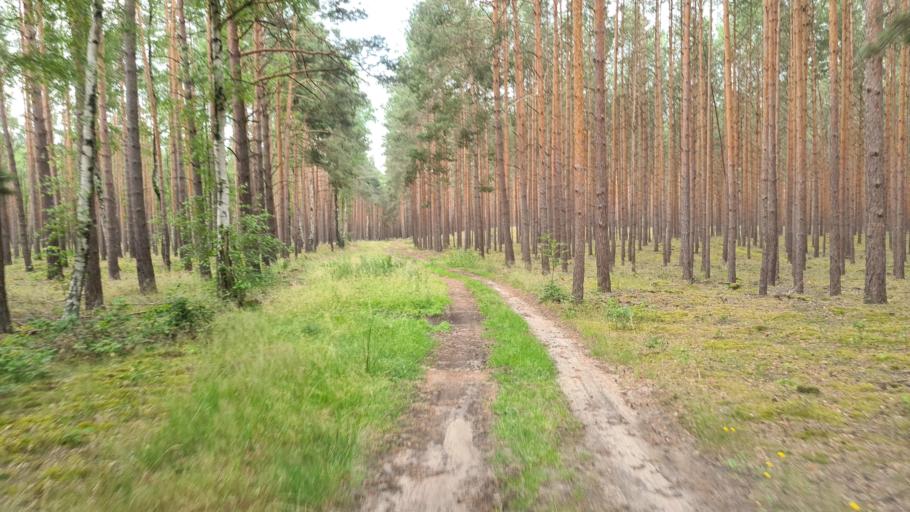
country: DE
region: Brandenburg
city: Crinitz
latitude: 51.7323
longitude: 13.7190
